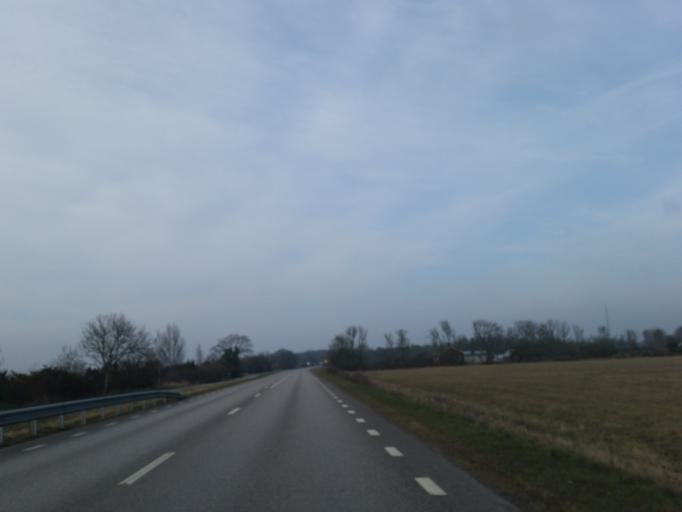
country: SE
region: Kalmar
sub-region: Borgholms Kommun
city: Borgholm
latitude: 56.8923
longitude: 16.7324
